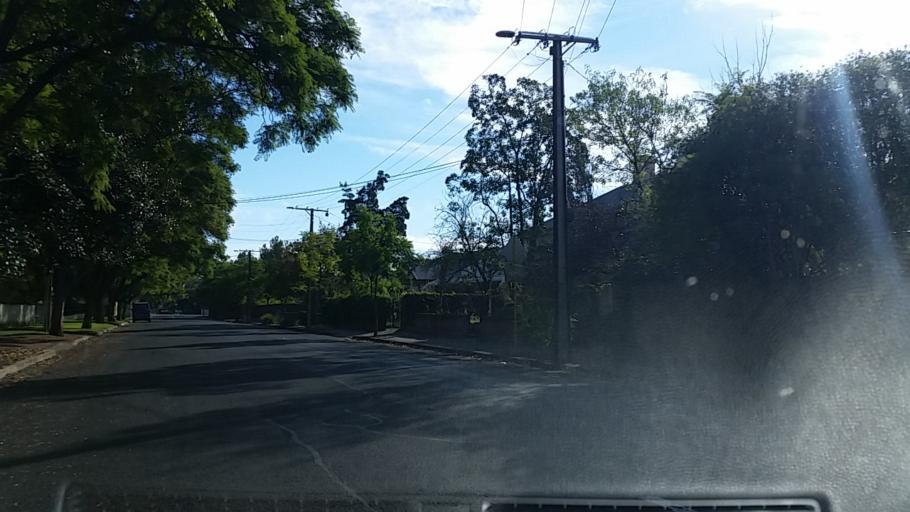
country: AU
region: South Australia
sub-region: Unley
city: Unley Park
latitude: -34.9675
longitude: 138.6026
